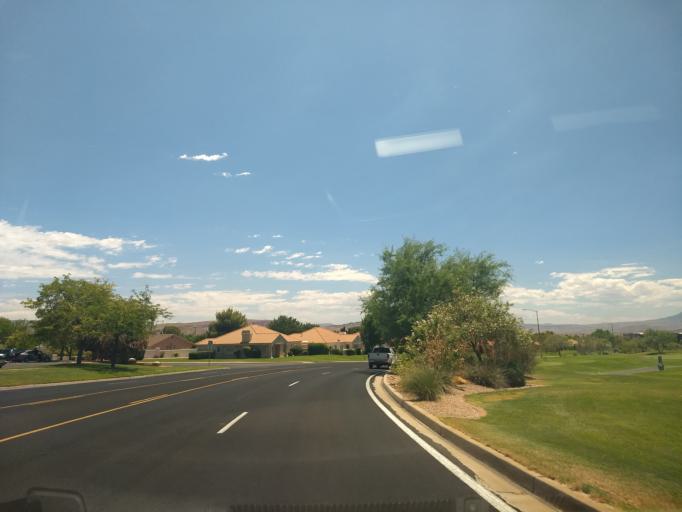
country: US
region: Utah
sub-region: Washington County
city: Washington
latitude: 37.1394
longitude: -113.5269
